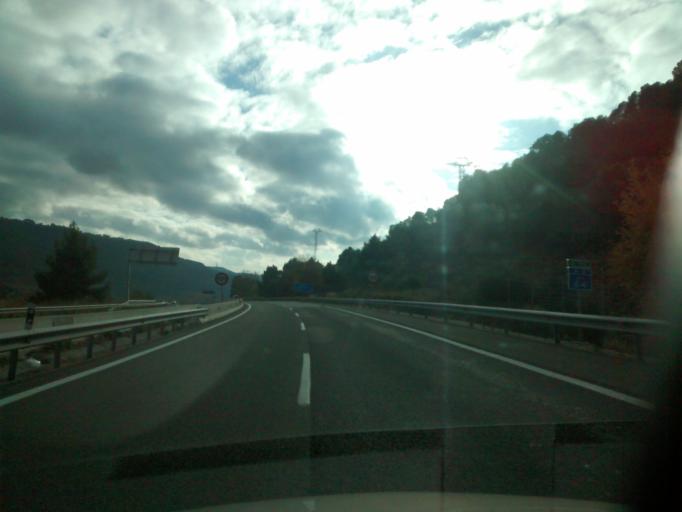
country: ES
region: Castille-La Mancha
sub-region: Provincia de Guadalajara
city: Tortola de Henares
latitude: 40.6820
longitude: -3.0950
